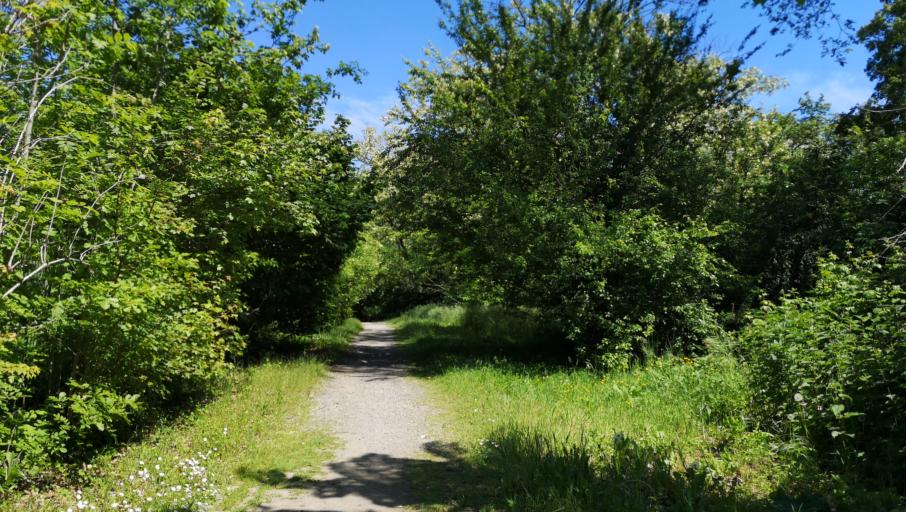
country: FR
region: Midi-Pyrenees
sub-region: Departement de la Haute-Garonne
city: Beauzelle
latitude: 43.6531
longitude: 1.3872
